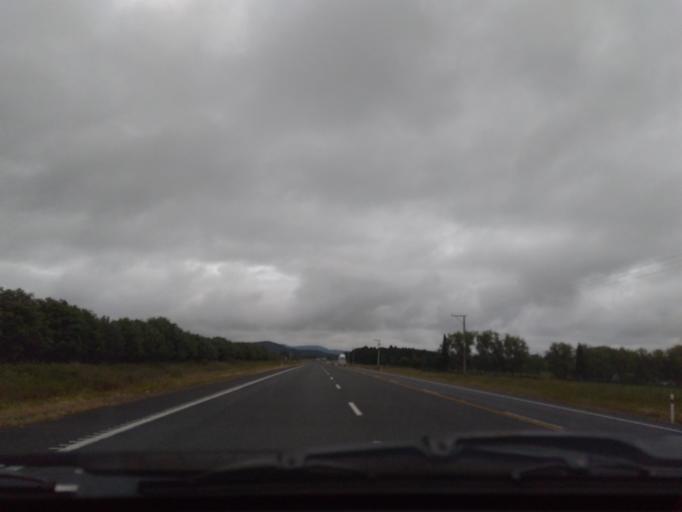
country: NZ
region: Northland
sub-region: Whangarei
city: Ruakaka
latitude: -36.0156
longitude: 174.4184
